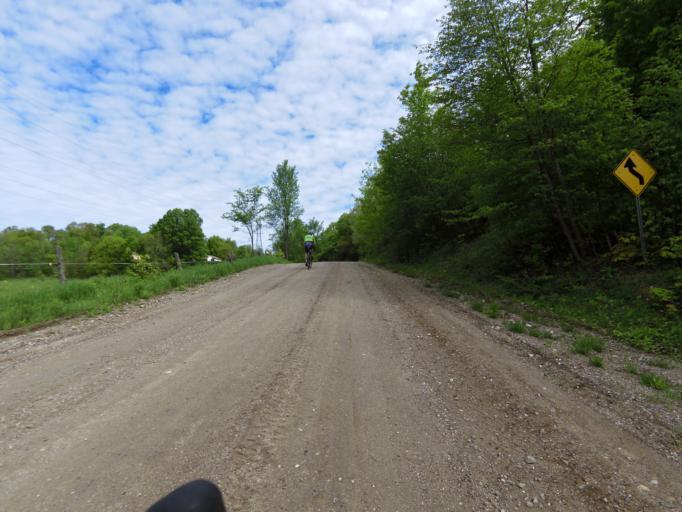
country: CA
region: Quebec
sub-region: Outaouais
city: Wakefield
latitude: 45.7934
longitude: -75.9172
